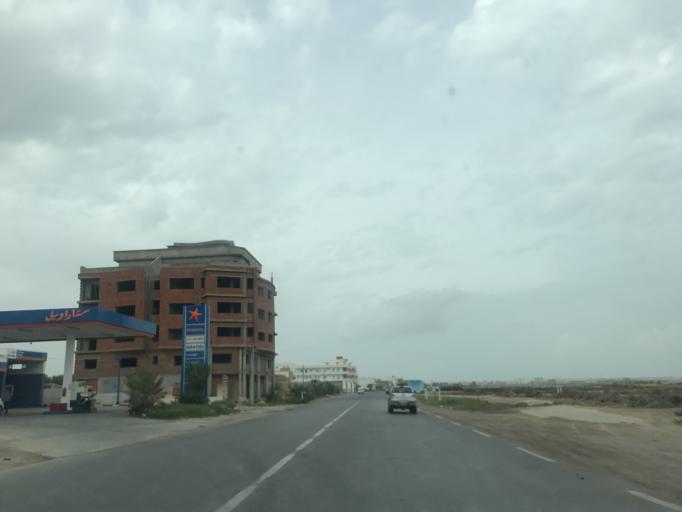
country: TN
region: Al Munastir
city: Qusaybat al Madyuni
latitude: 35.7015
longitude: 10.8280
